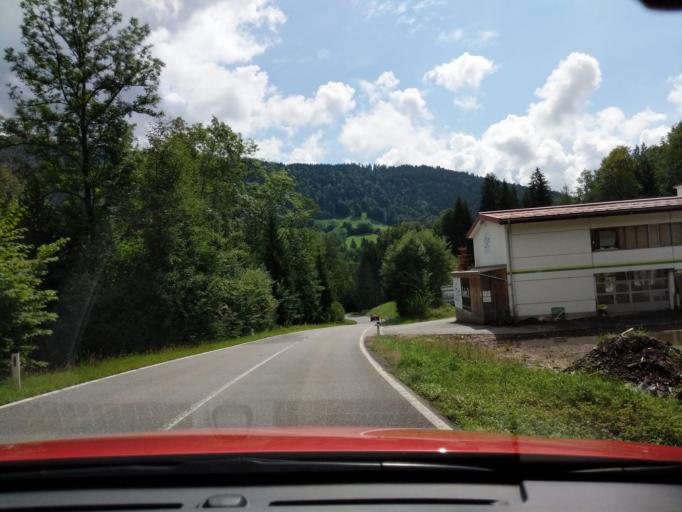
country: AT
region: Vorarlberg
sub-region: Politischer Bezirk Bregenz
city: Krumbach
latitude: 47.4903
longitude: 9.9369
